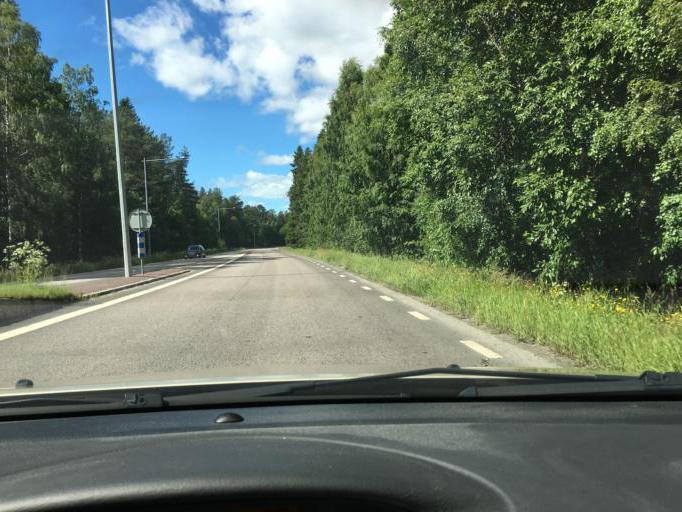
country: SE
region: Norrbotten
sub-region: Lulea Kommun
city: Bergnaset
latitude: 65.5775
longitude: 22.0935
